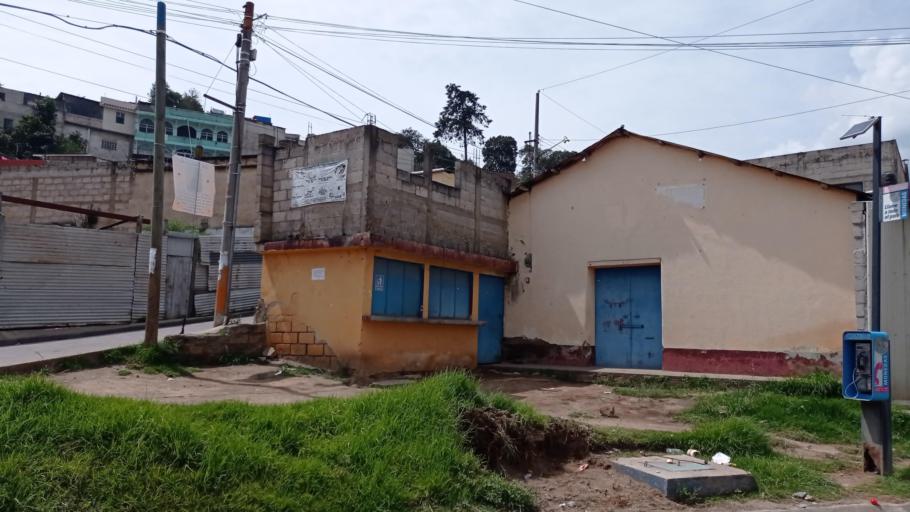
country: GT
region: Quetzaltenango
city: Quetzaltenango
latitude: 14.8471
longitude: -91.5020
